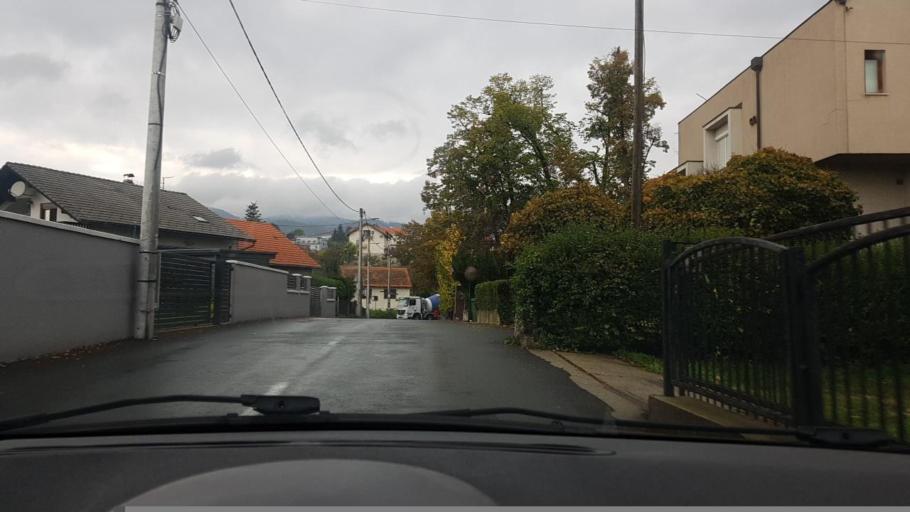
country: HR
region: Grad Zagreb
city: Zagreb
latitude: 45.8517
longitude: 15.9873
